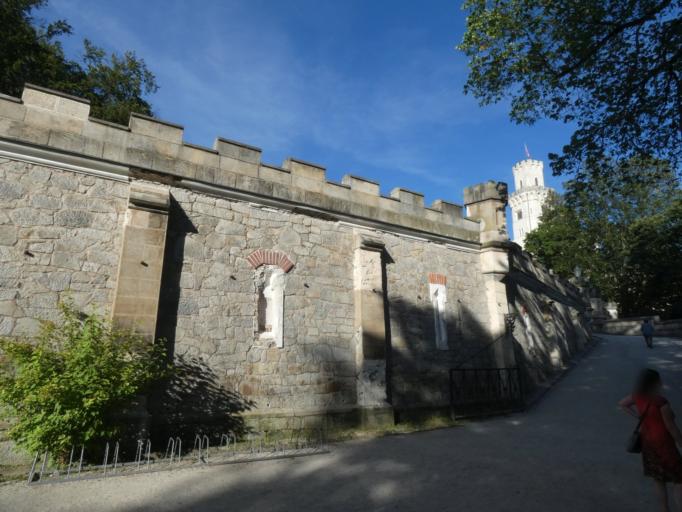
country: CZ
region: Jihocesky
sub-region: Okres Ceske Budejovice
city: Hluboka nad Vltavou
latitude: 49.0511
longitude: 14.4399
